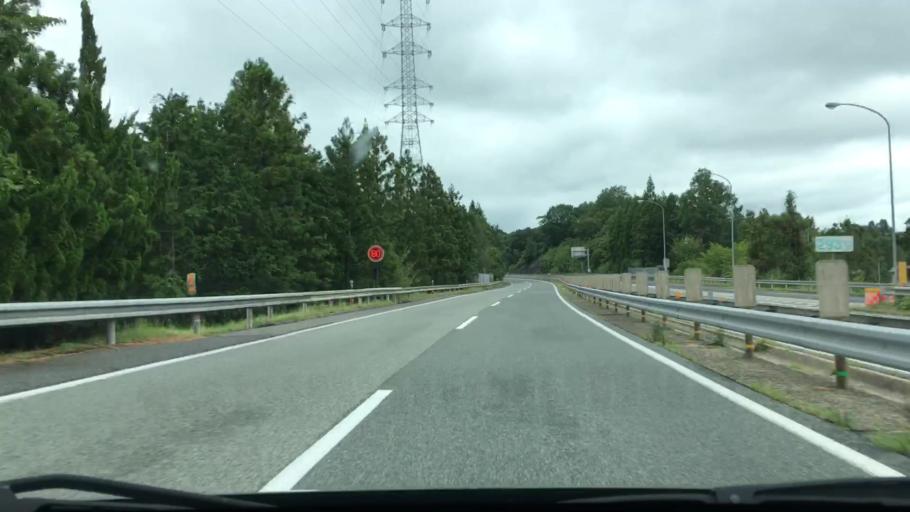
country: JP
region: Hiroshima
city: Miyoshi
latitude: 34.7863
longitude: 132.8598
